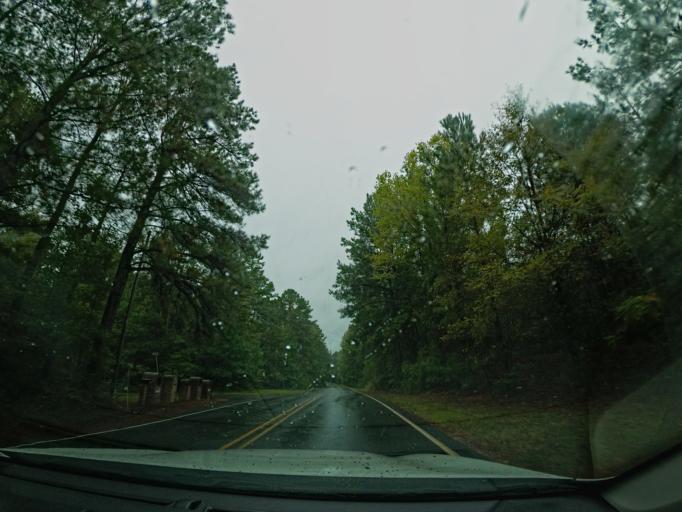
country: US
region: Louisiana
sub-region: Webster Parish
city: Minden
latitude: 32.6531
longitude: -93.2691
